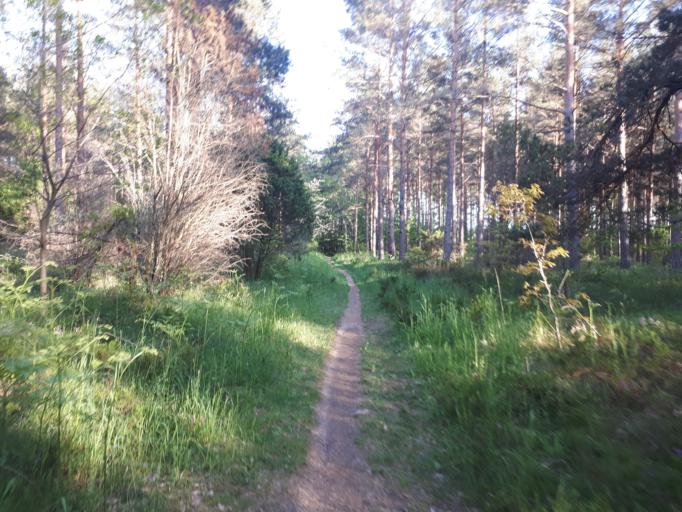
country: SE
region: Gotland
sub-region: Gotland
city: Visby
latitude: 57.6036
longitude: 18.2990
